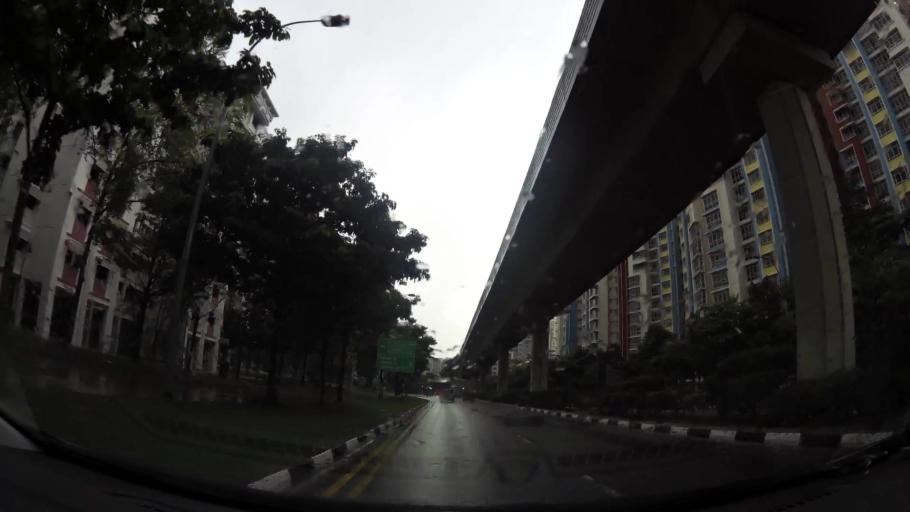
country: MY
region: Johor
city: Kampung Pasir Gudang Baru
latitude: 1.3855
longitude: 103.8962
